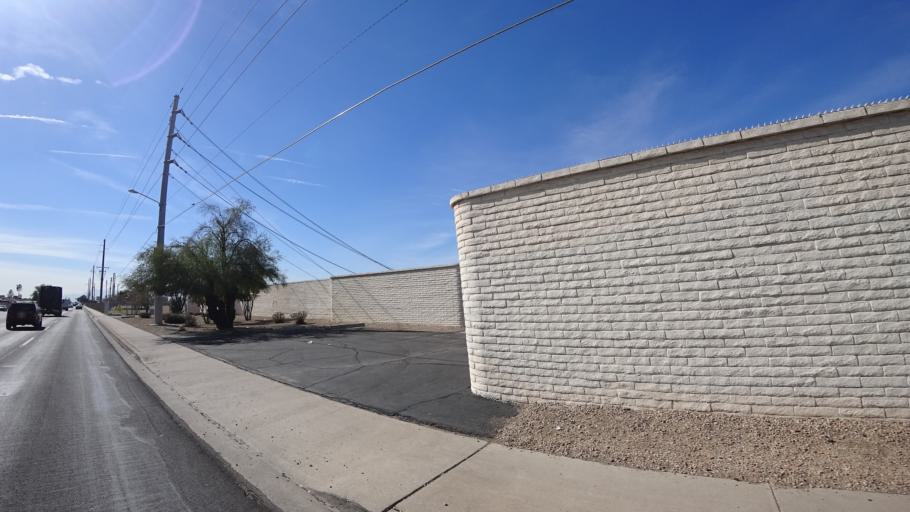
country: US
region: Arizona
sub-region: Maricopa County
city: Glendale
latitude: 33.4769
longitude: -112.1865
